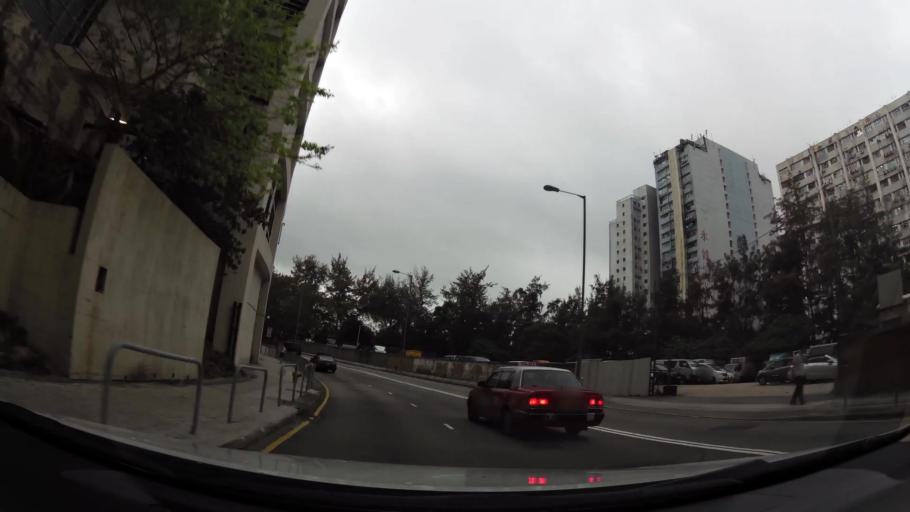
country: HK
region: Tsuen Wan
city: Tsuen Wan
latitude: 22.3596
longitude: 114.1206
